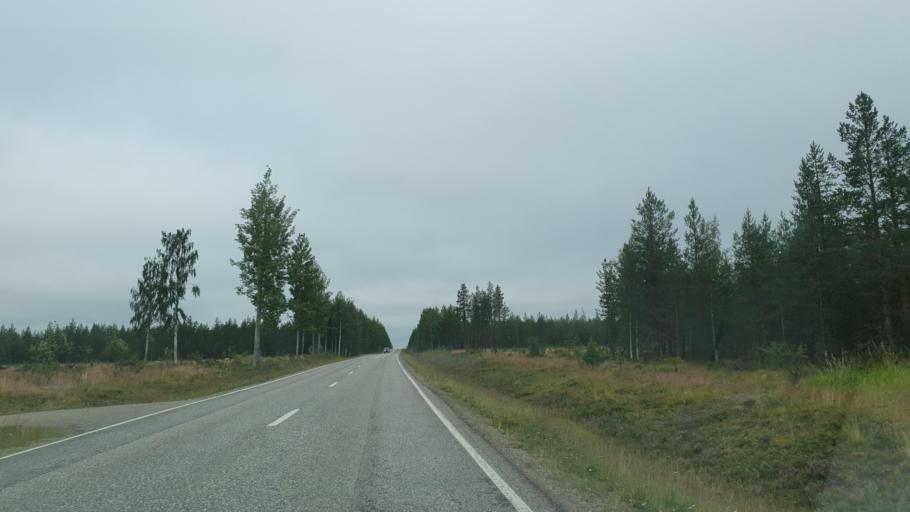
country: FI
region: Lapland
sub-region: Pohjois-Lappi
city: Sodankylae
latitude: 67.3977
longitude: 26.7142
